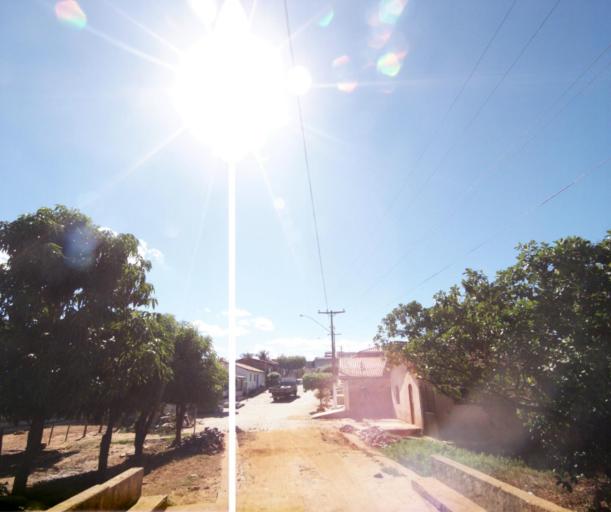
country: BR
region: Bahia
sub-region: Carinhanha
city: Carinhanha
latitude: -14.1788
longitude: -44.5293
